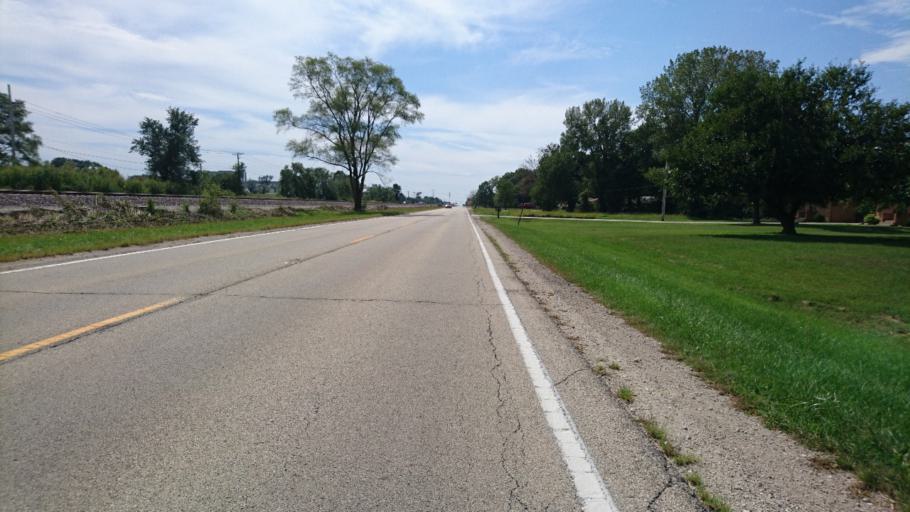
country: US
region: Illinois
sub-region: Will County
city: Braidwood
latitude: 41.2563
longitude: -88.2224
